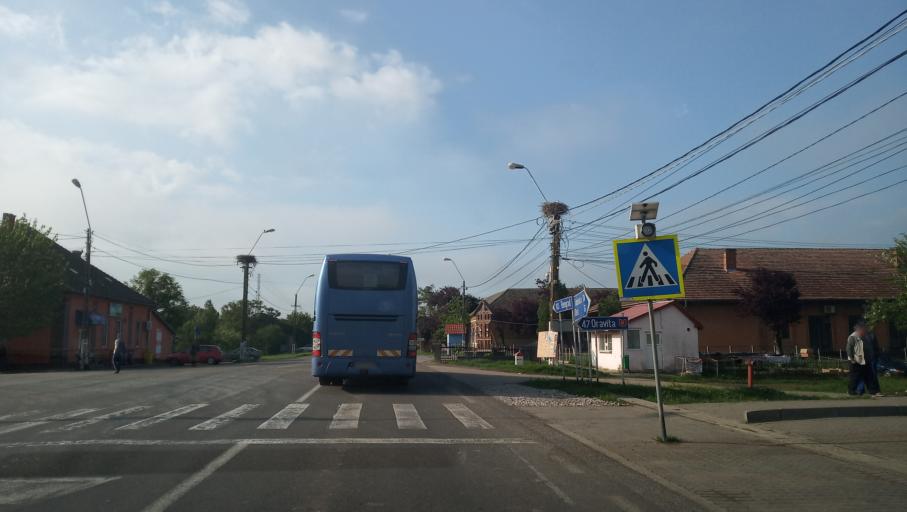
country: RO
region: Timis
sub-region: Comuna Moravita
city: Moravita
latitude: 45.2574
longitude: 21.2666
